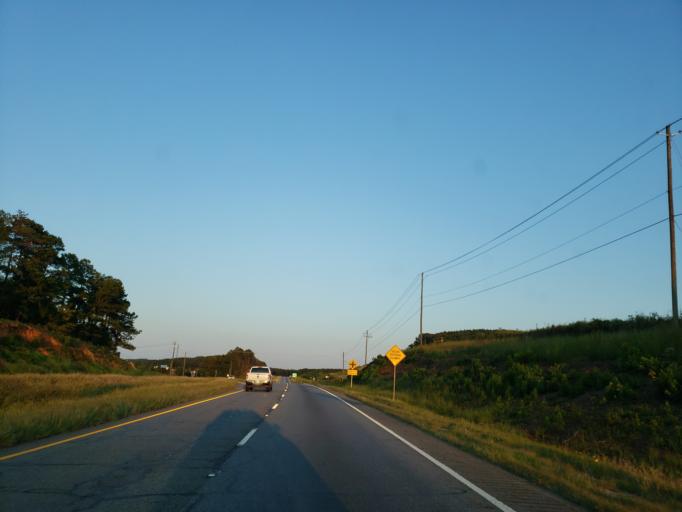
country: US
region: Georgia
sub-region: Bartow County
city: Cartersville
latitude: 34.2189
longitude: -84.8742
